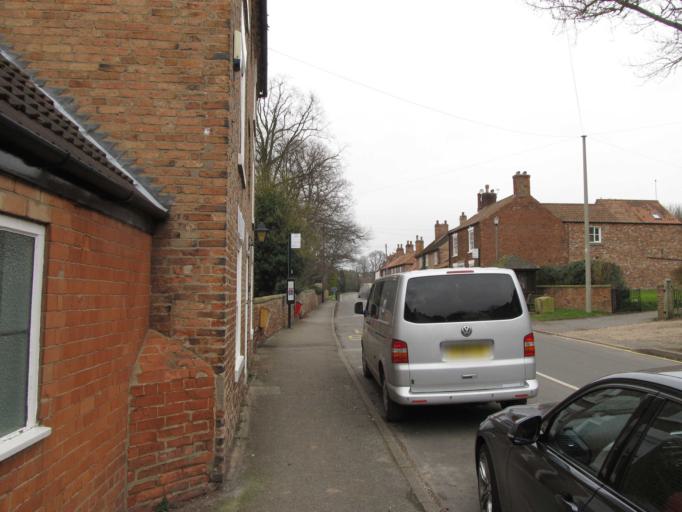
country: GB
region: England
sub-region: Nottinghamshire
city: Misterton
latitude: 53.4082
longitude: -0.8933
